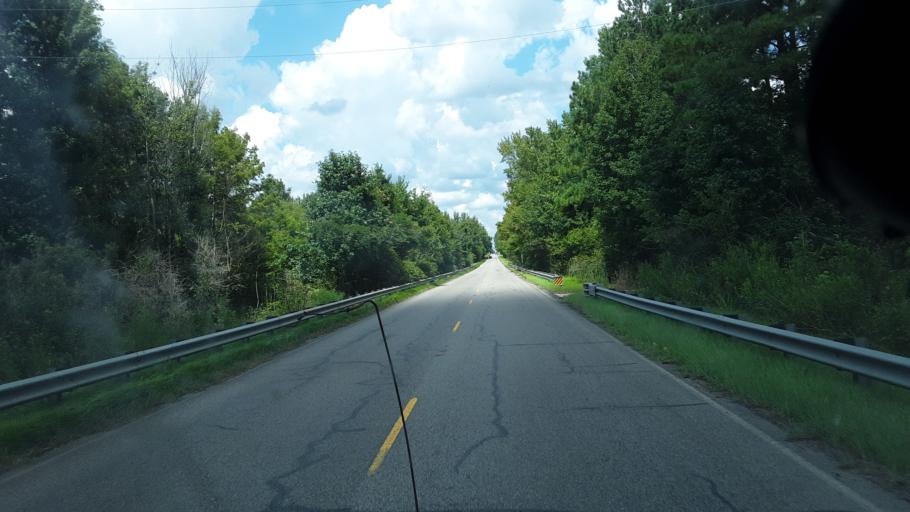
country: US
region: South Carolina
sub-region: Williamsburg County
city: Andrews
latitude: 33.5847
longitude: -79.4464
